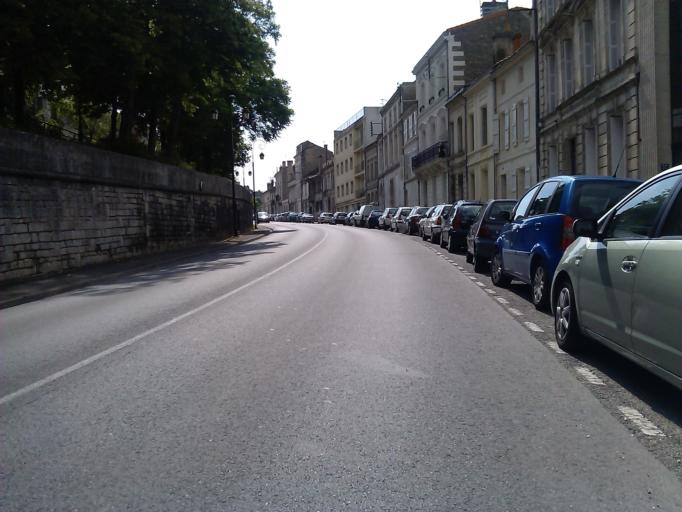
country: FR
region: Poitou-Charentes
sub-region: Departement de la Charente
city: Angouleme
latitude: 45.6496
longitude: 0.1475
